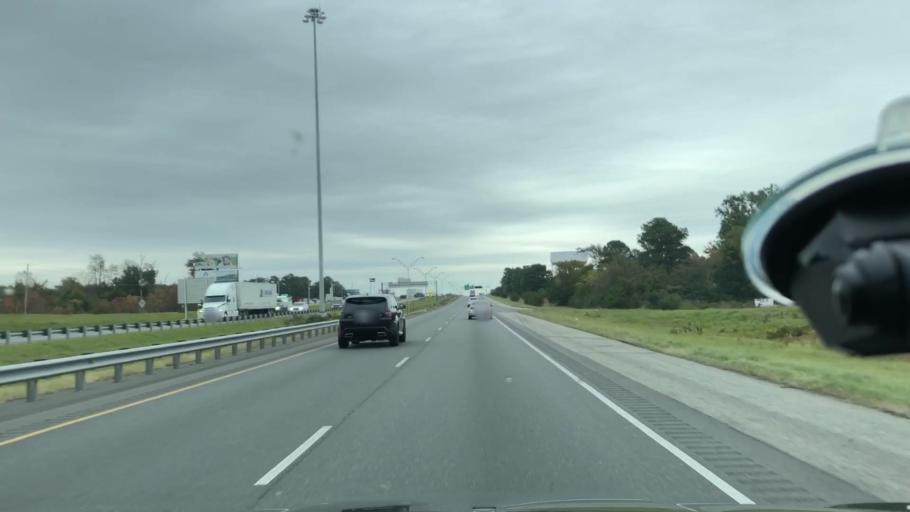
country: US
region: Arkansas
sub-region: Miller County
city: Texarkana
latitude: 33.4713
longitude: -94.0284
